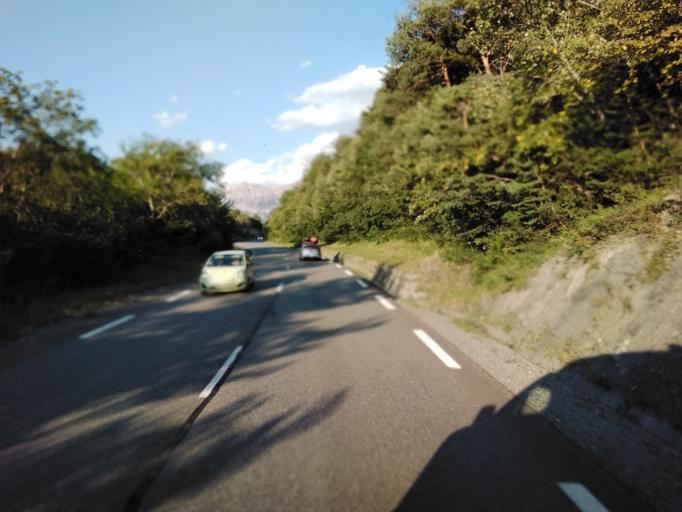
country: FR
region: Provence-Alpes-Cote d'Azur
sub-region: Departement des Hautes-Alpes
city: Chorges
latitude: 44.4558
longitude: 6.3065
